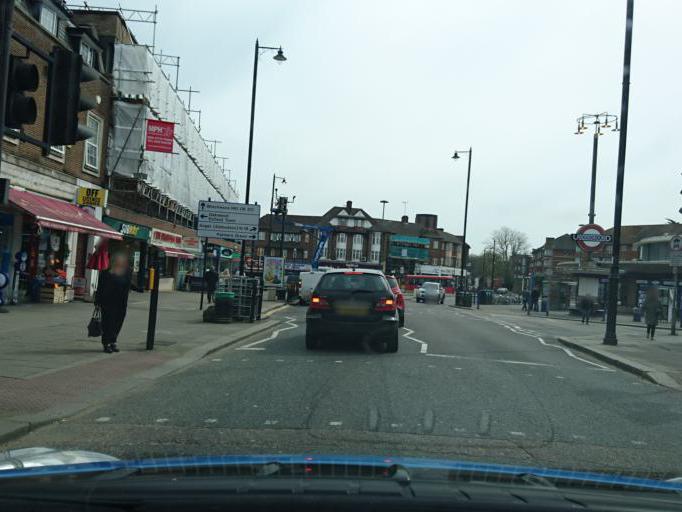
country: GB
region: England
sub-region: Greater London
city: Wood Green
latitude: 51.6328
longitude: -0.1284
